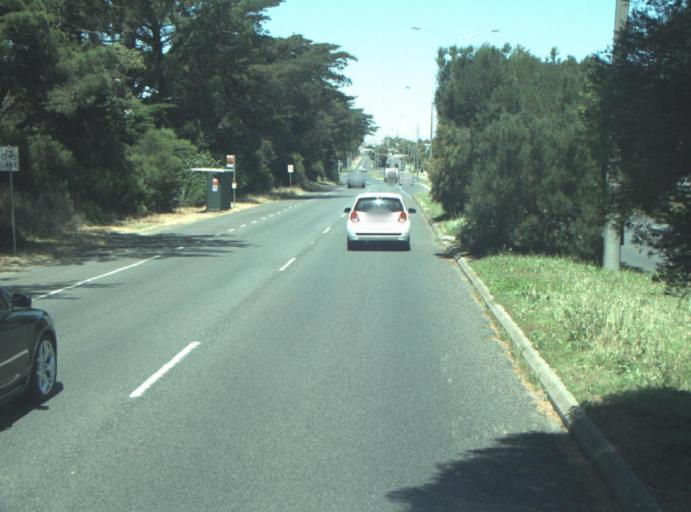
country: AU
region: Victoria
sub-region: Greater Geelong
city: Hamlyn Heights
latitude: -38.1248
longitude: 144.3376
